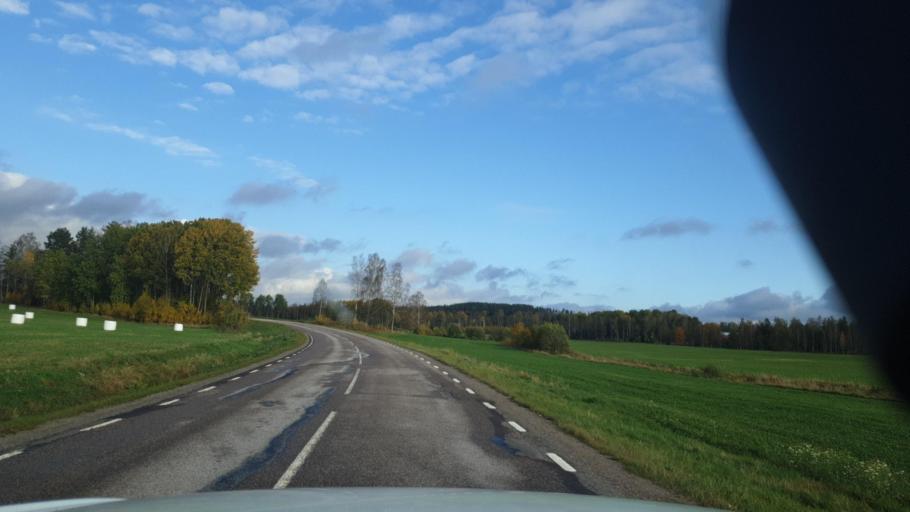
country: SE
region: Vaermland
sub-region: Arvika Kommun
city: Arvika
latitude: 59.4964
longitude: 12.6855
